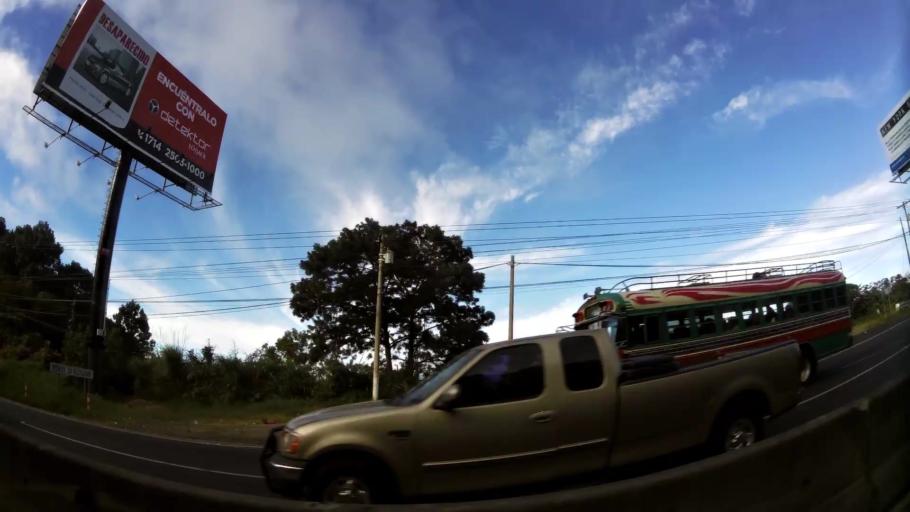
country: GT
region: Guatemala
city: Santa Catarina Pinula
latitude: 14.5791
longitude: -90.4777
